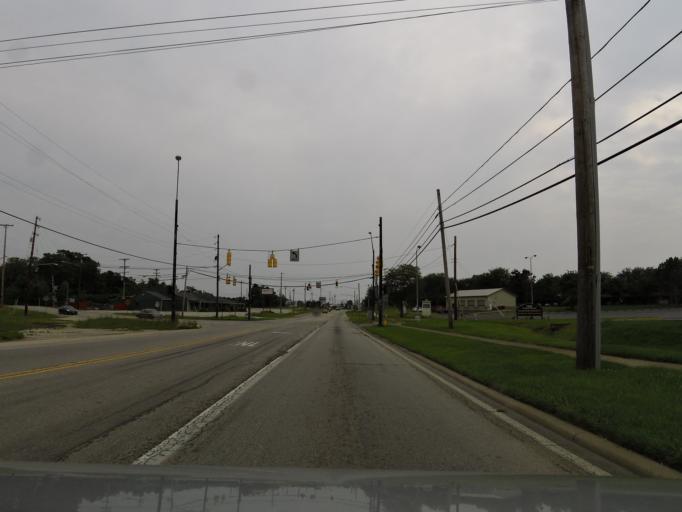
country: US
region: Ohio
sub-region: Clinton County
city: Wilmington
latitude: 39.4326
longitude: -83.8309
